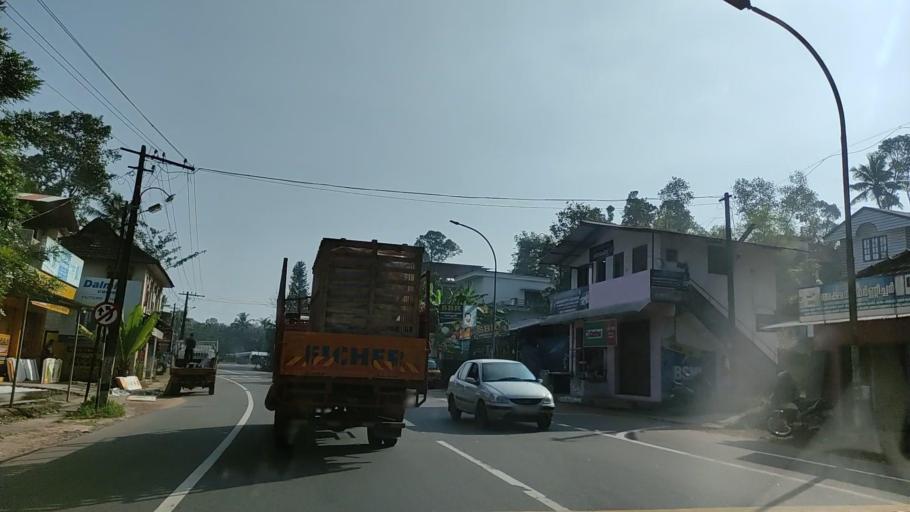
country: IN
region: Kerala
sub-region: Kollam
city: Punalur
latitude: 8.9729
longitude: 76.8266
